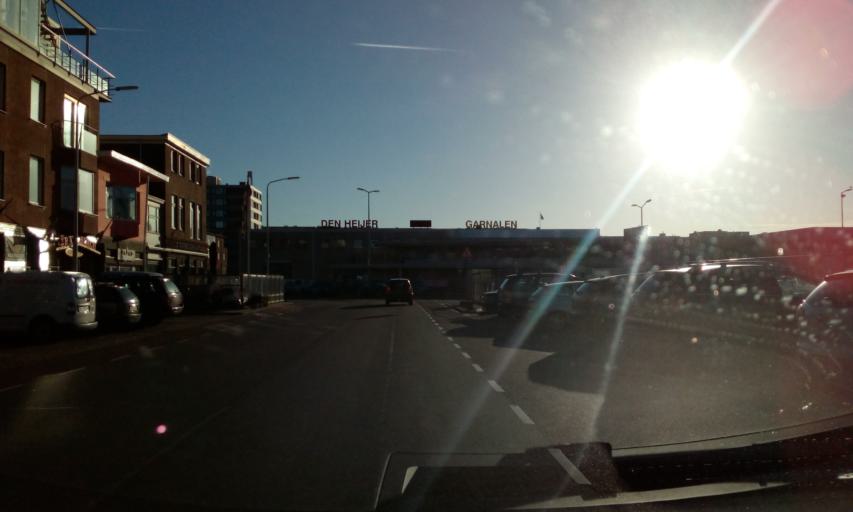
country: NL
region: South Holland
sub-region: Gemeente Den Haag
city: Scheveningen
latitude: 52.1016
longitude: 4.2685
